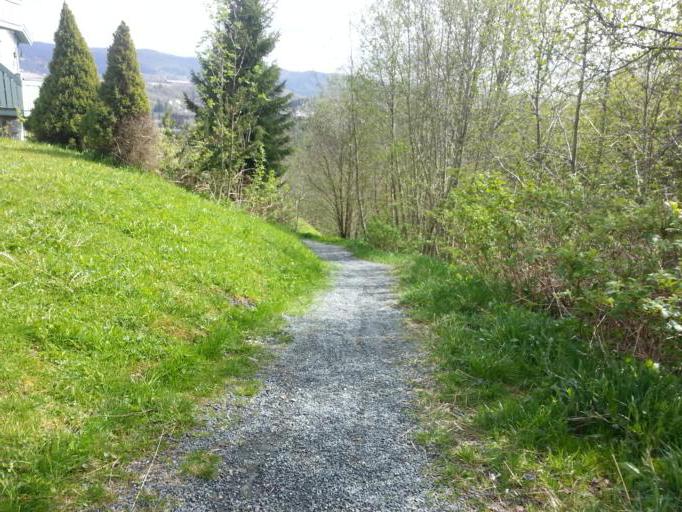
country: NO
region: Sor-Trondelag
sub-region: Trondheim
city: Trondheim
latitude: 63.3886
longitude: 10.3664
